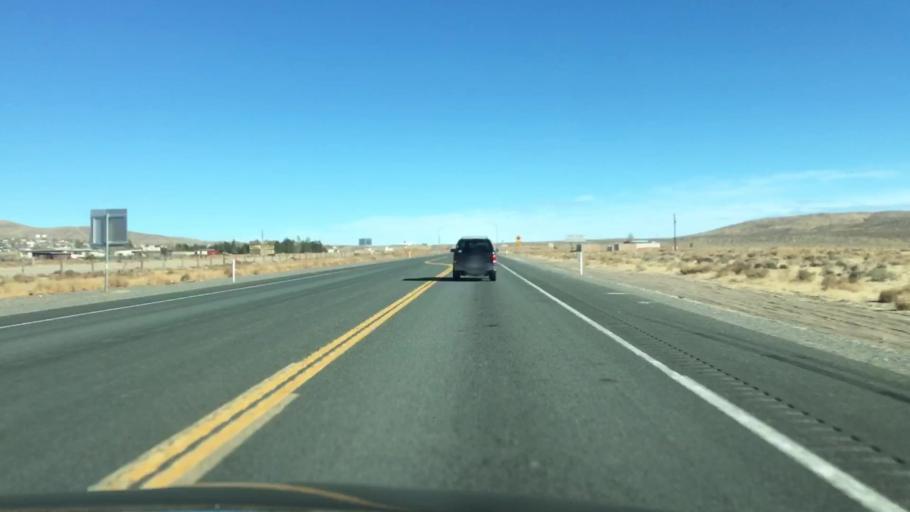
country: US
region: Nevada
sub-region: Lyon County
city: Stagecoach
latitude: 39.3618
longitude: -119.3739
